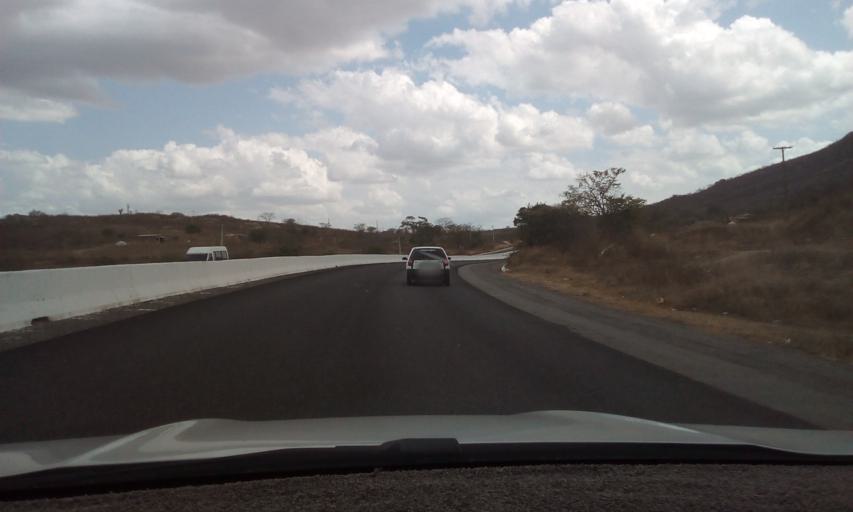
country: BR
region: Pernambuco
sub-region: Toritama
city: Toritama
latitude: -8.0916
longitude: -36.0334
